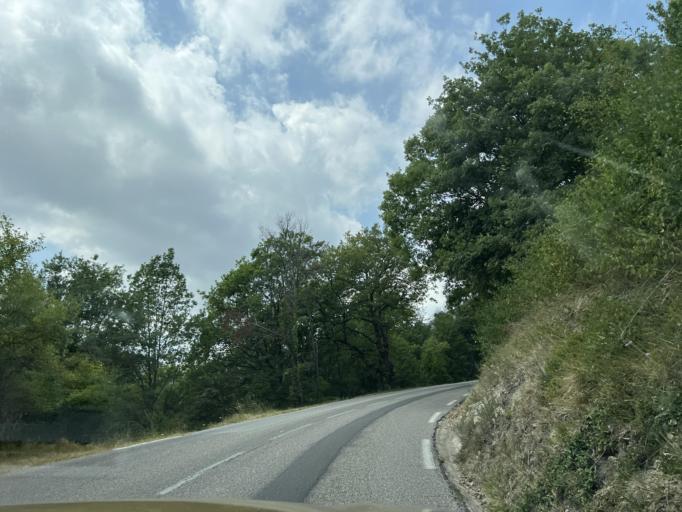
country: FR
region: Provence-Alpes-Cote d'Azur
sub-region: Departement des Alpes-Maritimes
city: Tourrettes-sur-Loup
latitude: 43.7944
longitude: 6.9639
